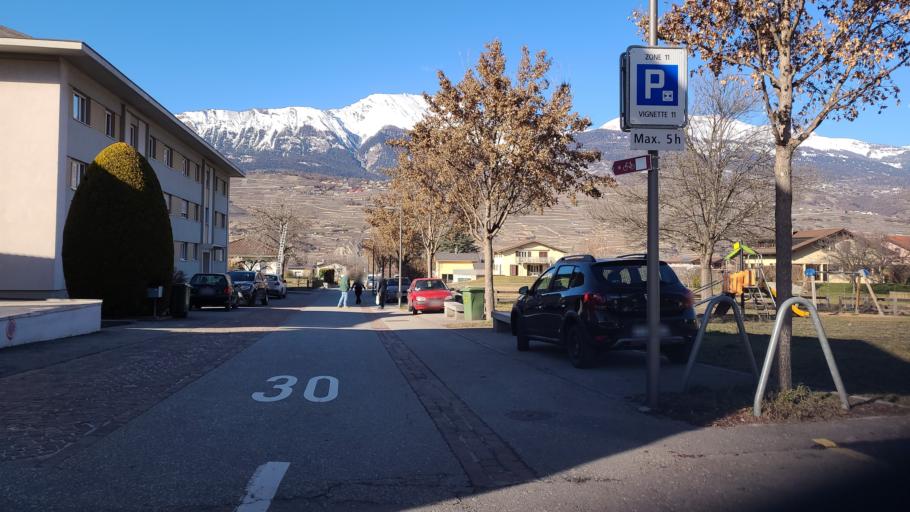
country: CH
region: Valais
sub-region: Herens District
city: Vex
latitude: 46.2343
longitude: 7.4025
